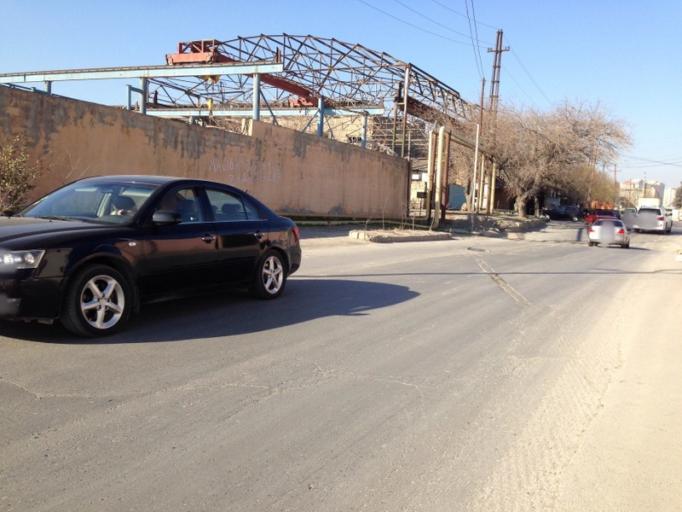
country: AZ
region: Baki
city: Baku
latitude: 40.4218
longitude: 49.8640
